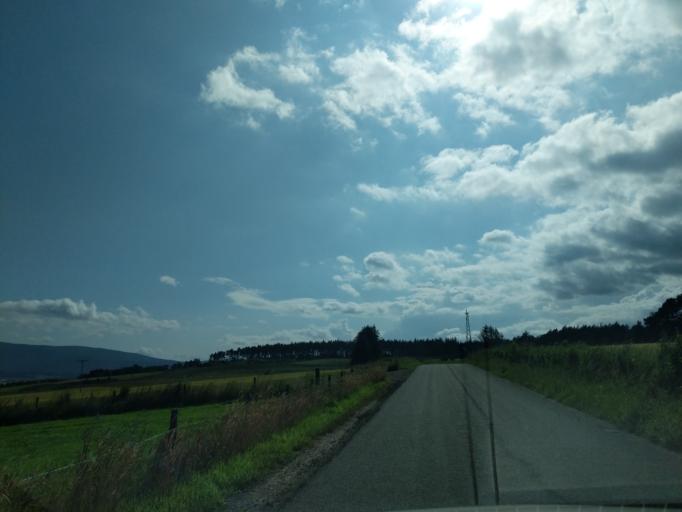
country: GB
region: Scotland
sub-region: Moray
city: Rothes
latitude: 57.4865
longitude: -3.2236
